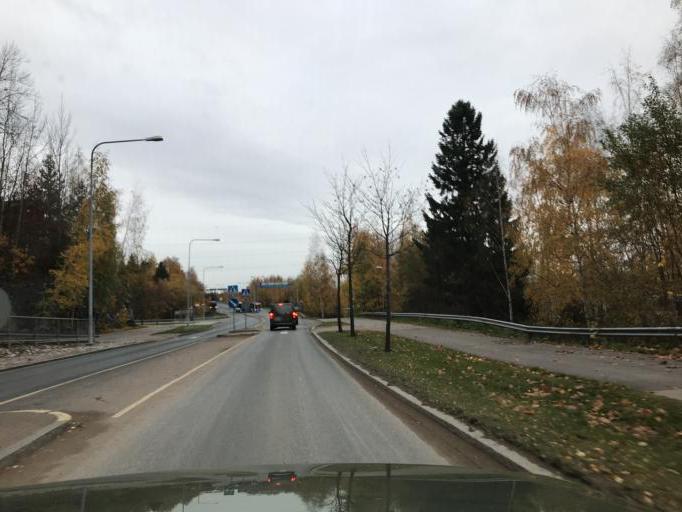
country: FI
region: Uusimaa
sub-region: Helsinki
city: Vantaa
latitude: 60.2740
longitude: 25.0768
